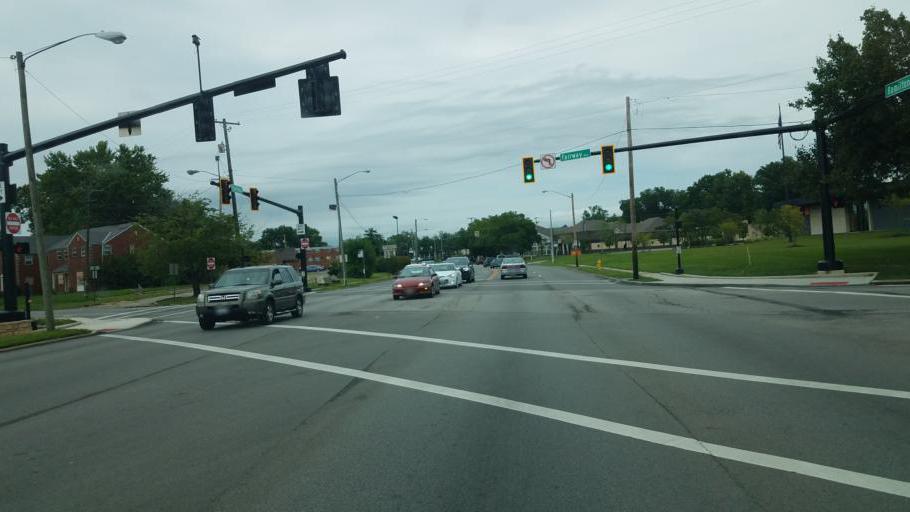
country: US
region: Ohio
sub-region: Franklin County
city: Whitehall
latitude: 39.9729
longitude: -82.8748
